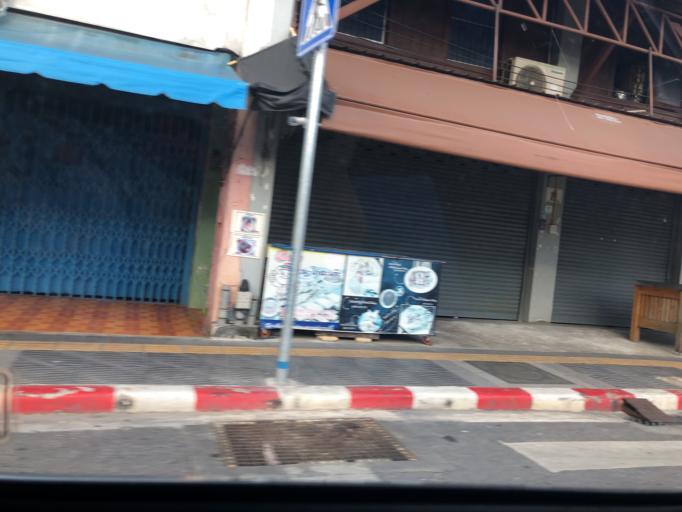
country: TH
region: Phuket
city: Ban Talat Nua
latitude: 7.8849
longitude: 98.3908
